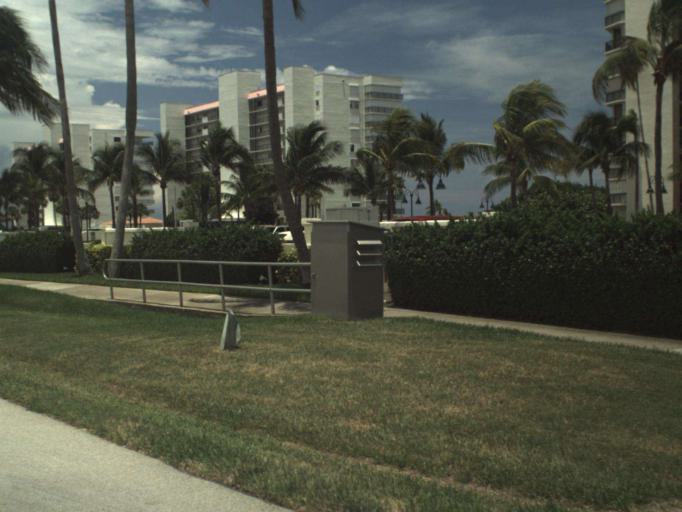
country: US
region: Florida
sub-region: Saint Lucie County
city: Hutchinson Island South
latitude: 27.2916
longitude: -80.2148
